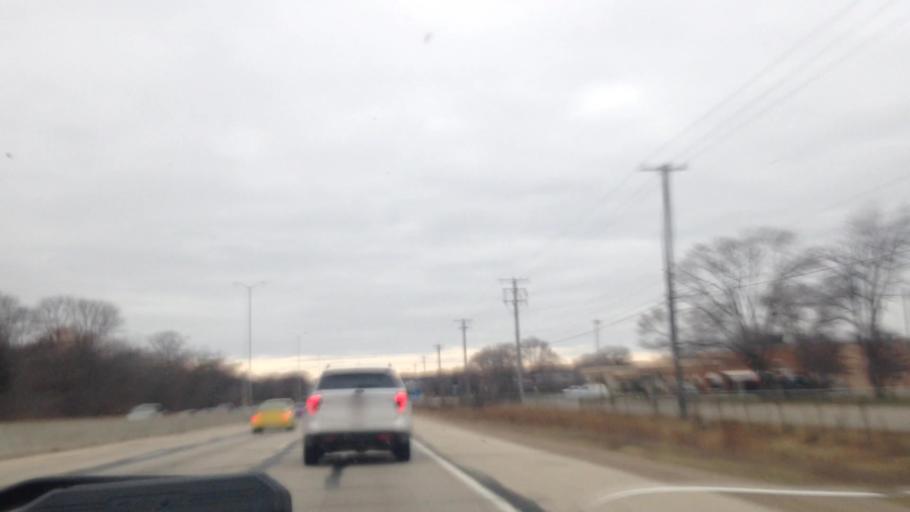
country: US
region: Wisconsin
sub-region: Waukesha County
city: Menomonee Falls
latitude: 43.1696
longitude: -88.0768
